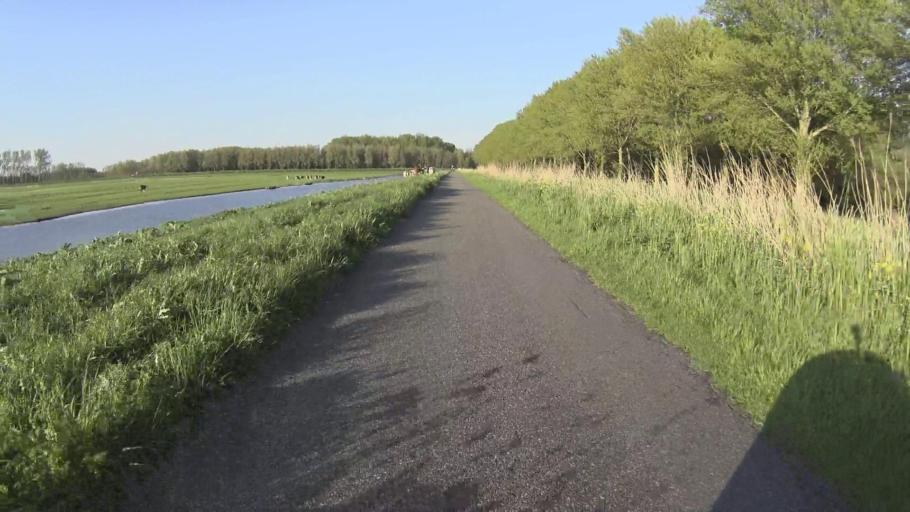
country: NL
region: South Holland
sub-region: Gemeente Pijnacker-Nootdorp
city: Pijnacker
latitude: 52.0249
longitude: 4.3996
